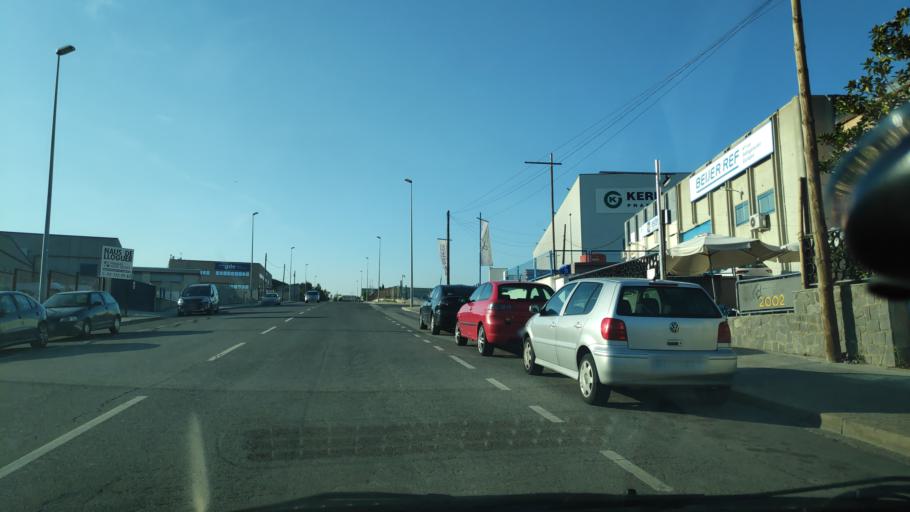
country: ES
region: Catalonia
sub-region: Provincia de Barcelona
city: Terrassa
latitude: 41.5373
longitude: 2.0317
